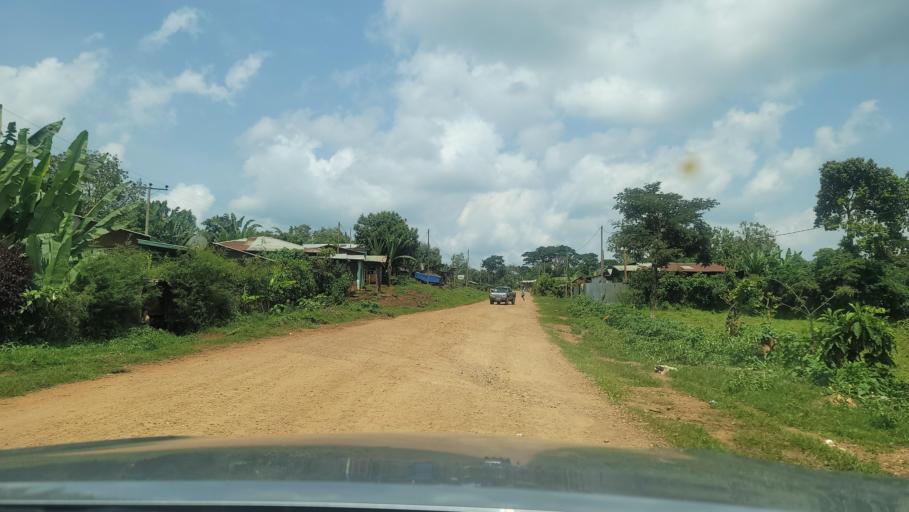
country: ET
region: Oromiya
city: Agaro
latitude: 7.7945
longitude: 36.4499
